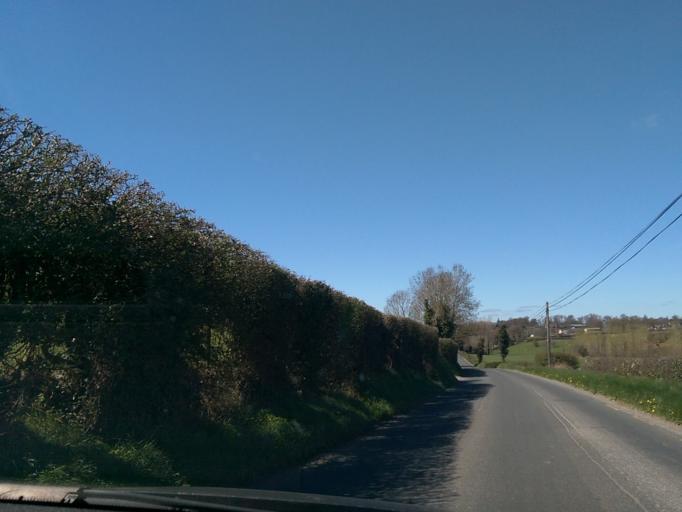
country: IE
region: Leinster
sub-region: Wicklow
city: Baltinglass
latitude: 52.8970
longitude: -6.6000
